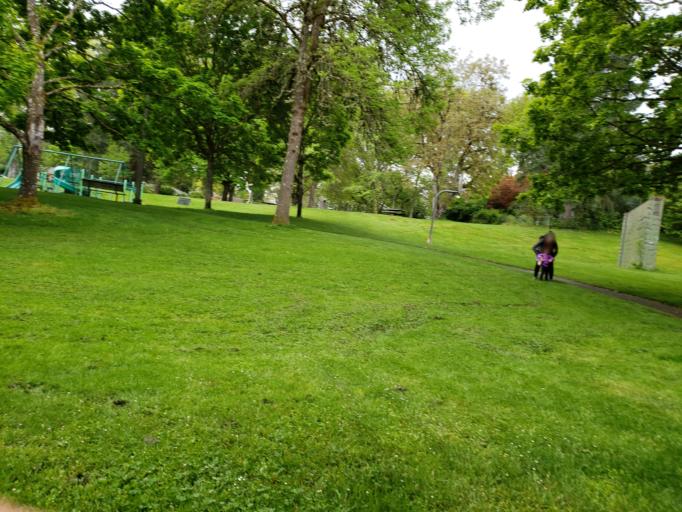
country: US
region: Oregon
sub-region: Washington County
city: Raleigh Hills
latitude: 45.4810
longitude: -122.7329
